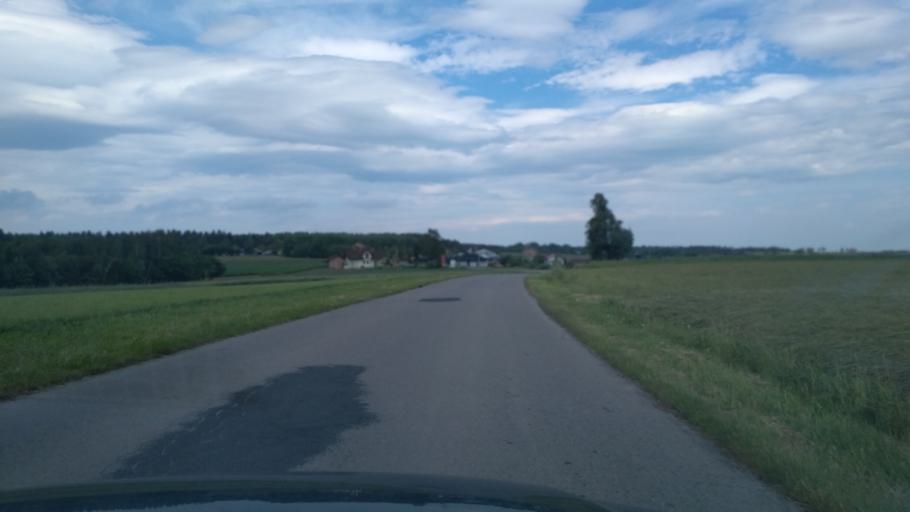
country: PL
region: Subcarpathian Voivodeship
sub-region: Powiat ropczycko-sedziszowski
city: Wielopole Skrzynskie
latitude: 49.9969
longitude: 21.6129
